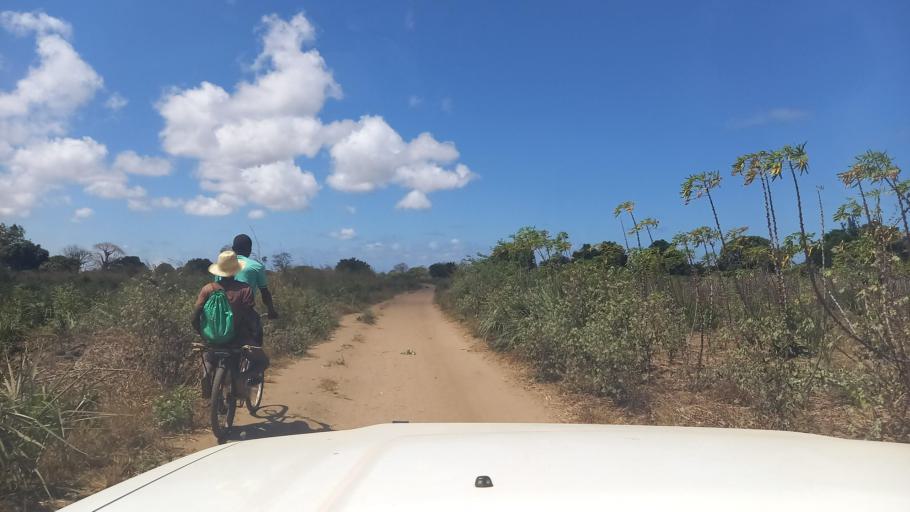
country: MZ
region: Cabo Delgado
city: Pemba
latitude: -13.4249
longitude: 40.4994
